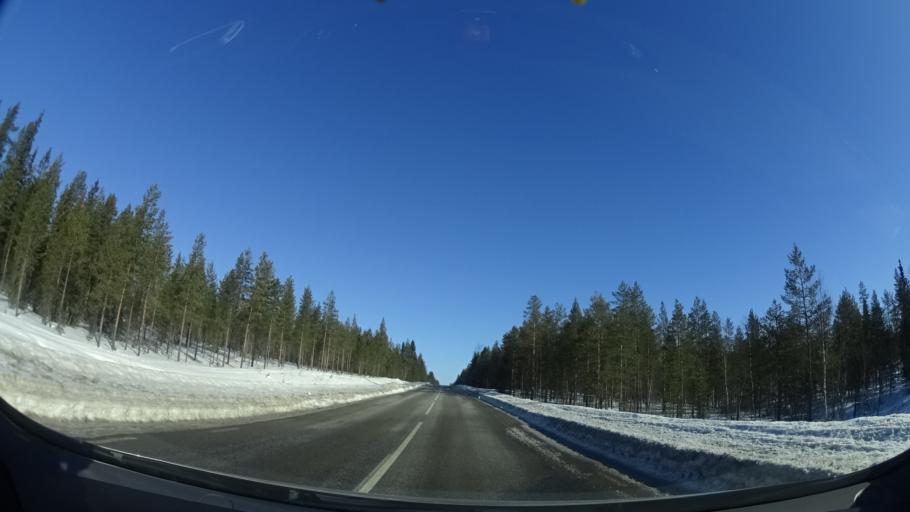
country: SE
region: Vaesterbotten
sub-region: Skelleftea Kommun
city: Langsele
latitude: 65.1345
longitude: 20.1584
